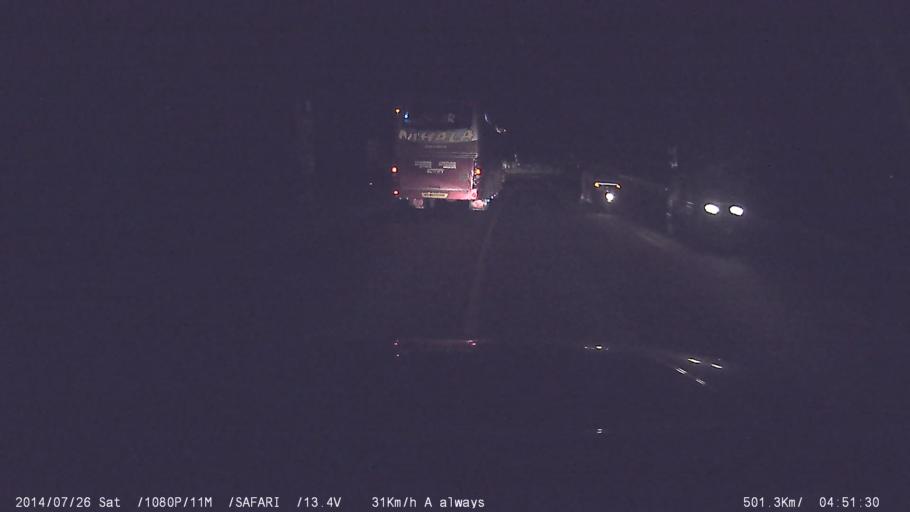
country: IN
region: Kerala
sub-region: Ernakulam
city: Angamali
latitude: 10.1603
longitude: 76.4428
